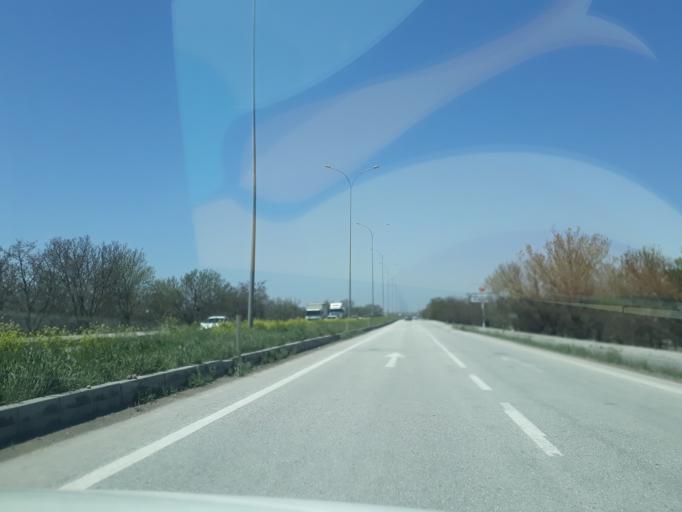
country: TR
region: Konya
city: Karapinar
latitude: 37.7142
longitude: 33.5232
